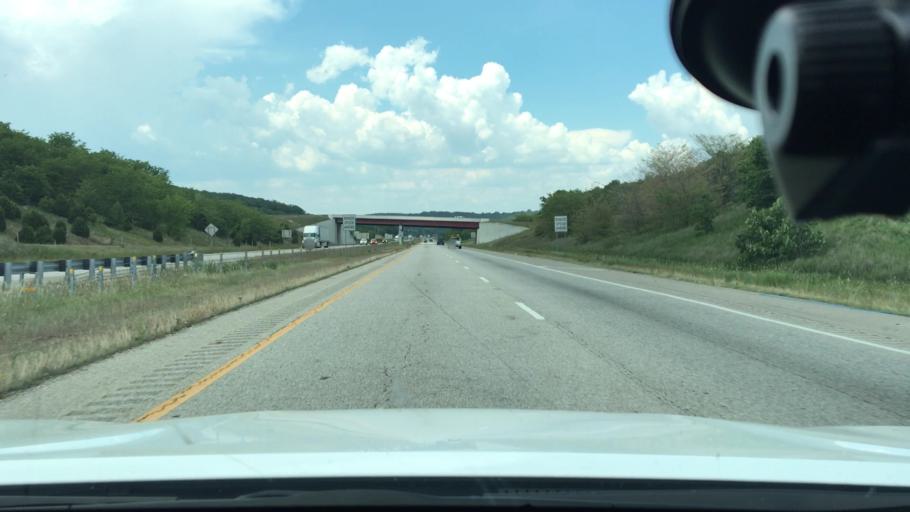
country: US
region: Arkansas
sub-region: Washington County
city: Fayetteville
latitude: 36.0347
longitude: -94.1883
